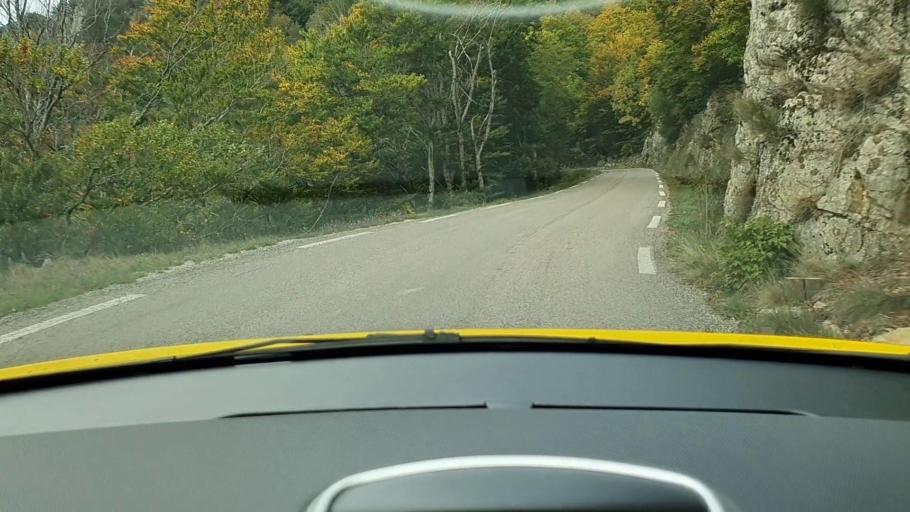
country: FR
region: Languedoc-Roussillon
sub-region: Departement du Gard
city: Le Vigan
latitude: 44.0402
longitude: 3.5651
